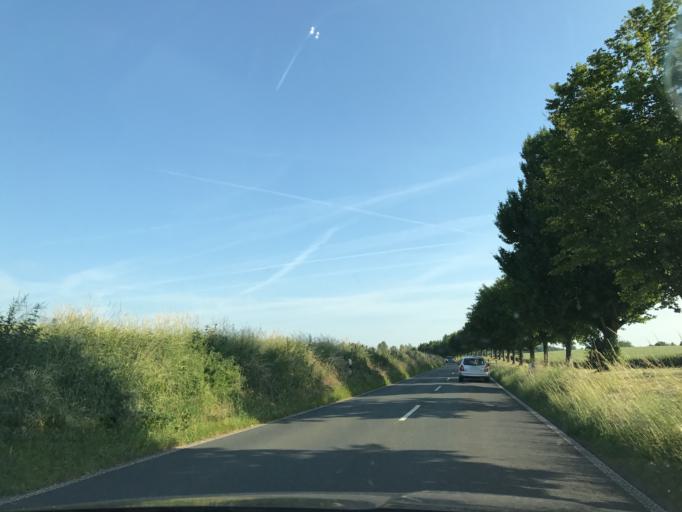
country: DE
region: North Rhine-Westphalia
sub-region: Regierungsbezirk Dusseldorf
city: Heiligenhaus
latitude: 51.3881
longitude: 6.9777
